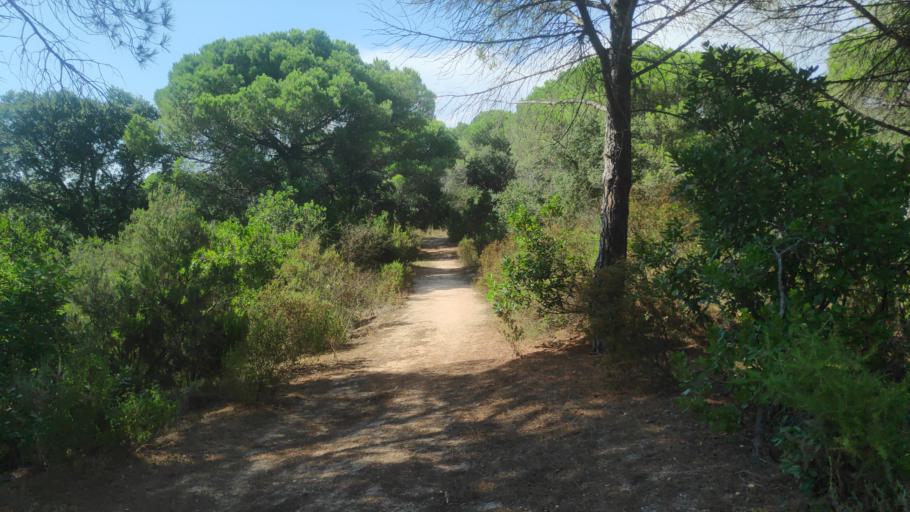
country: ES
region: Catalonia
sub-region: Provincia de Girona
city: Lloret de Mar
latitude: 41.7257
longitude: 2.8299
